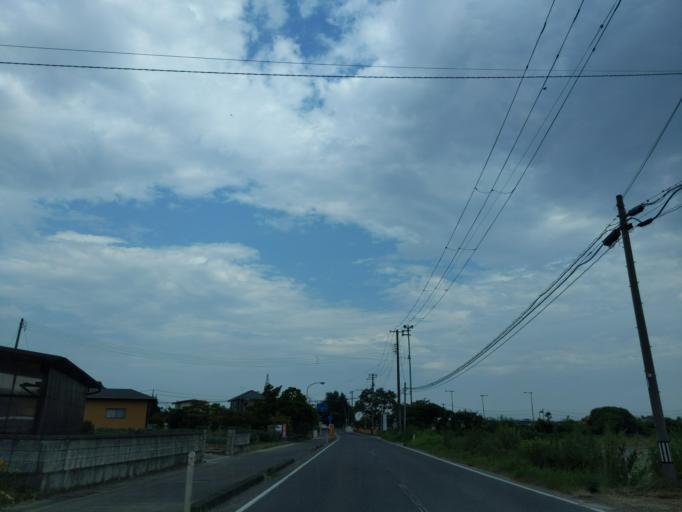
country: JP
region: Miyagi
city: Tomiya
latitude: 38.4324
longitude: 140.8886
